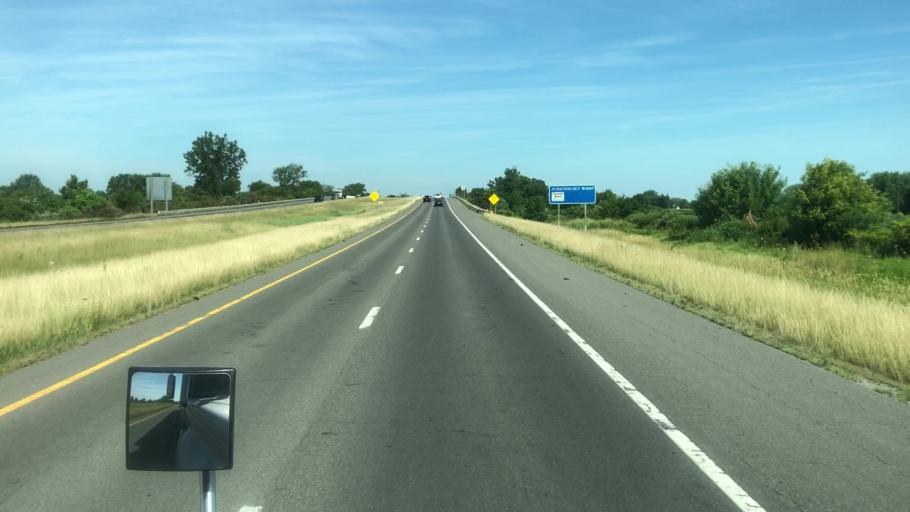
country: US
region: Ohio
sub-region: Erie County
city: Sandusky
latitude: 41.4253
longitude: -82.7665
